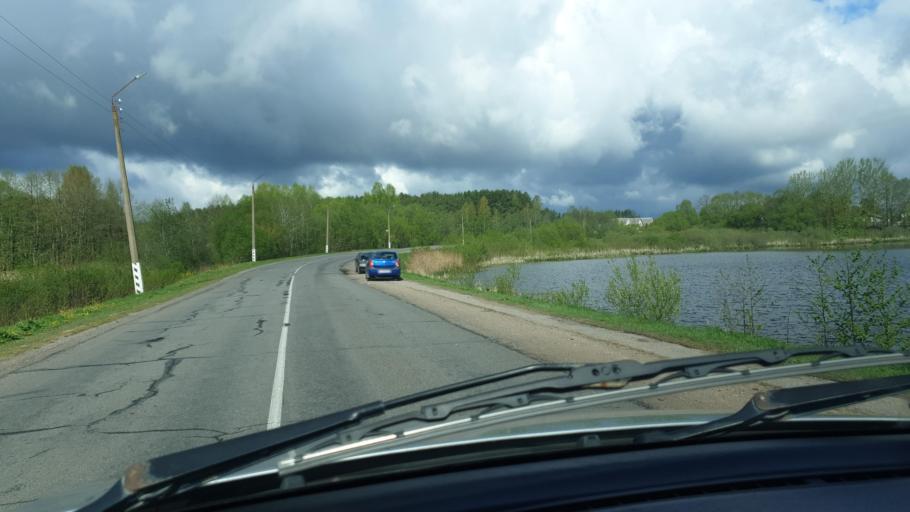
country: BY
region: Vitebsk
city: Lyepyel'
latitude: 54.8771
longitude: 28.6646
